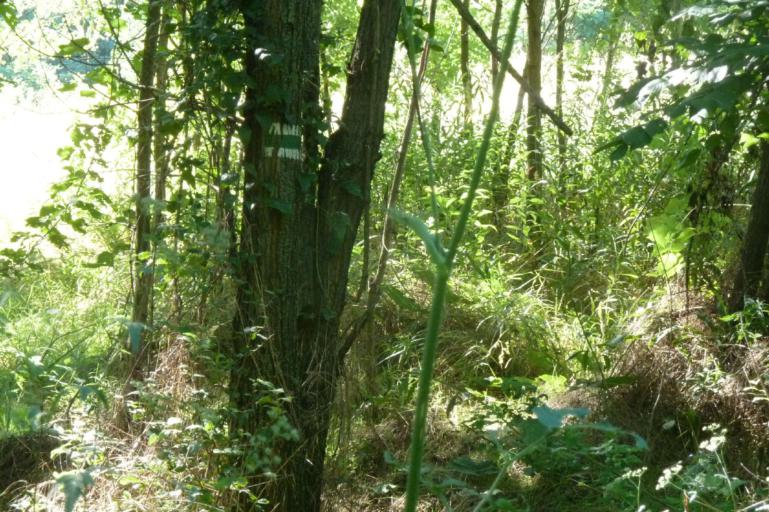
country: HU
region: Somogy
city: Karad
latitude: 46.5977
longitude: 17.8957
